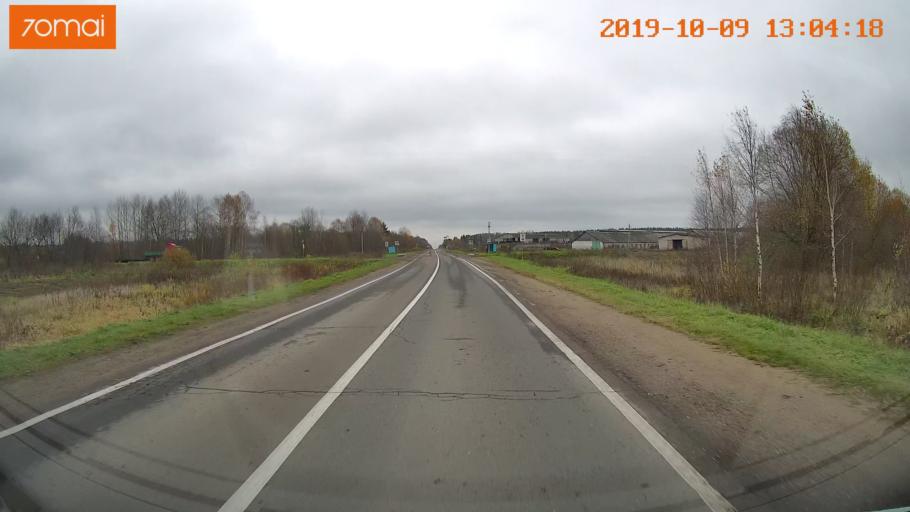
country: RU
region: Jaroslavl
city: Lyubim
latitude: 58.3585
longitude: 40.5507
